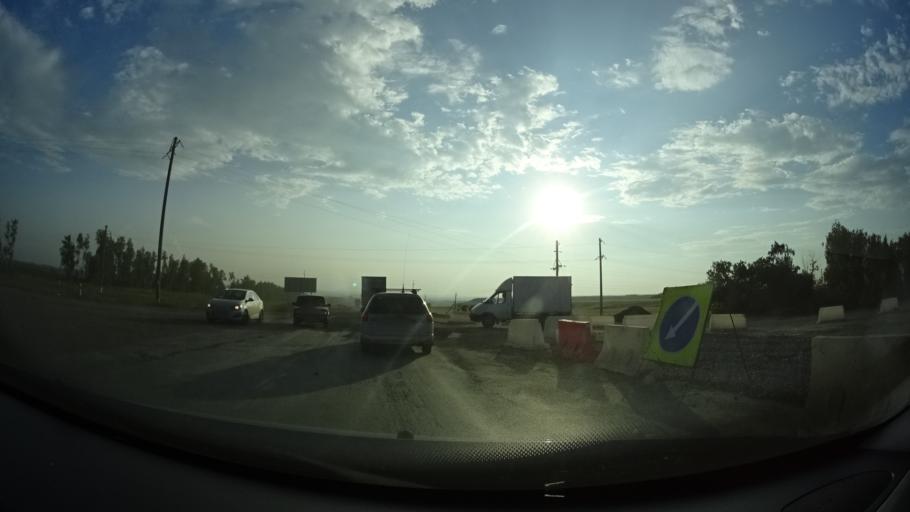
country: RU
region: Samara
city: Kamyshla
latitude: 54.0644
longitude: 52.1358
